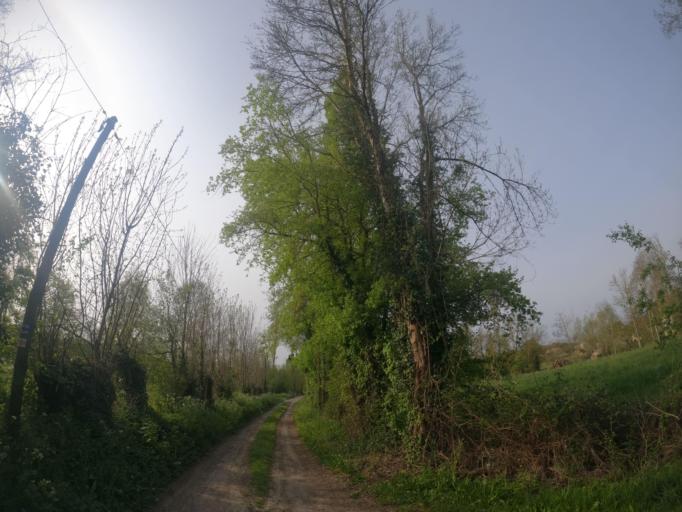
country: FR
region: Poitou-Charentes
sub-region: Departement des Deux-Sevres
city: Saint-Jean-de-Thouars
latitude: 46.9231
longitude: -0.1802
